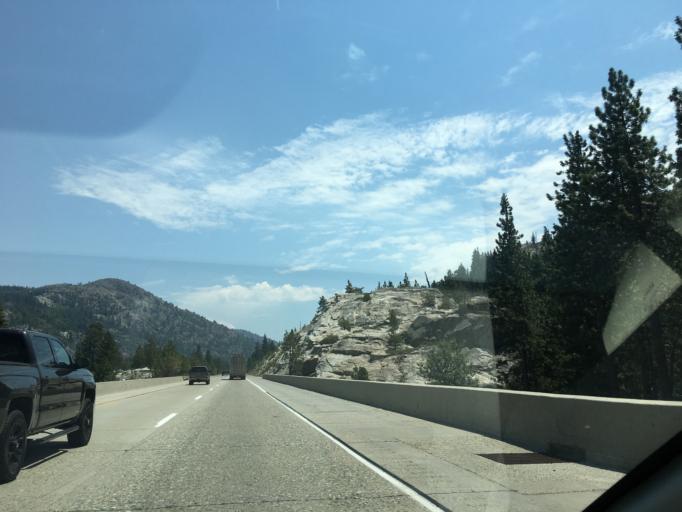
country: US
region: California
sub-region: Sierra County
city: Downieville
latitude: 39.3292
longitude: -120.5827
